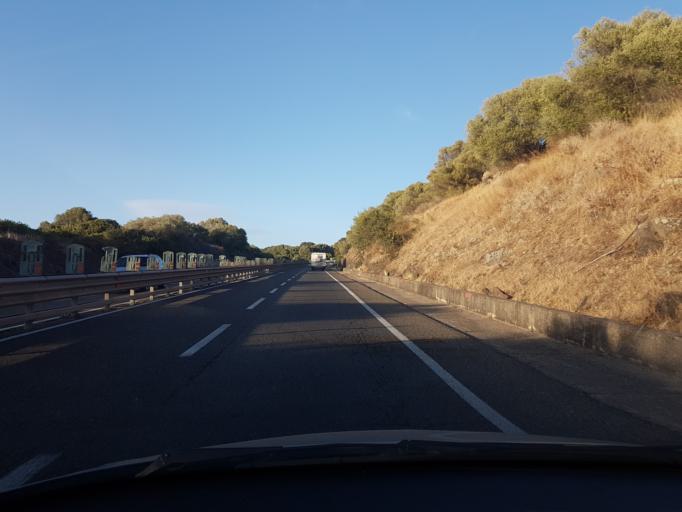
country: IT
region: Sardinia
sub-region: Provincia di Oristano
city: Paulilatino
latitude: 40.0573
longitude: 8.7176
